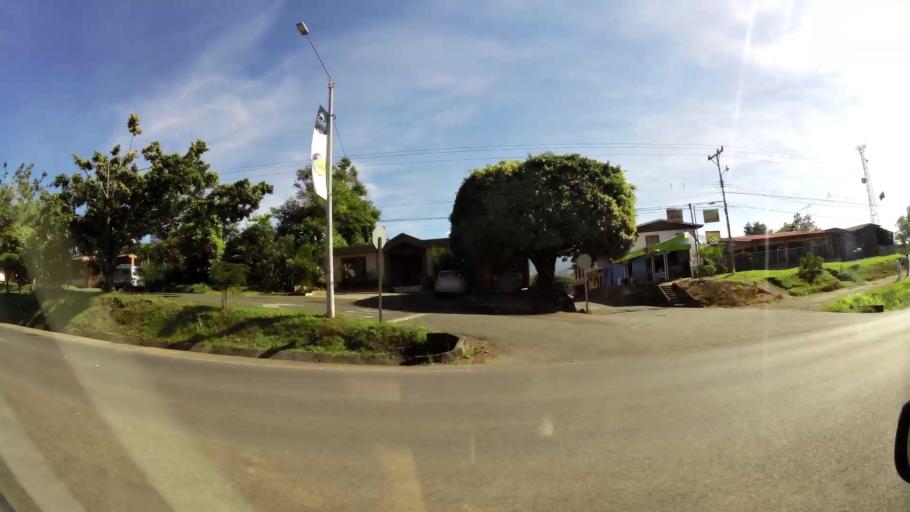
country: CR
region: San Jose
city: San Isidro
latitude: 9.3795
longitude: -83.7051
